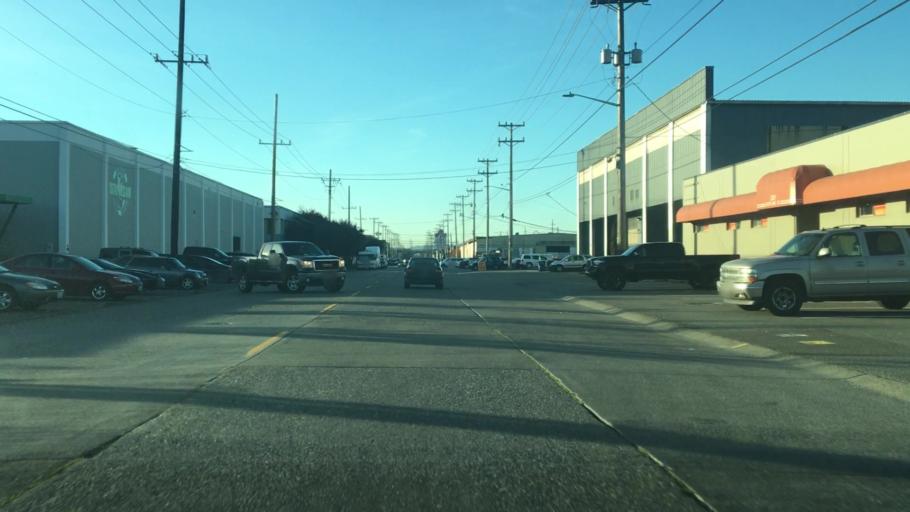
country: US
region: Washington
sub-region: King County
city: Seattle
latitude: 47.5840
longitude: -122.3260
